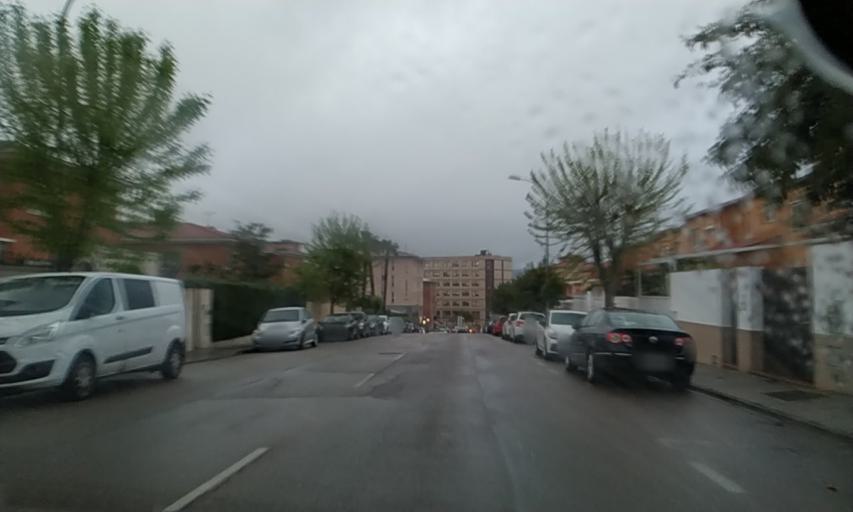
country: ES
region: Extremadura
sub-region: Provincia de Badajoz
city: Merida
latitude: 38.9101
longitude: -6.3627
